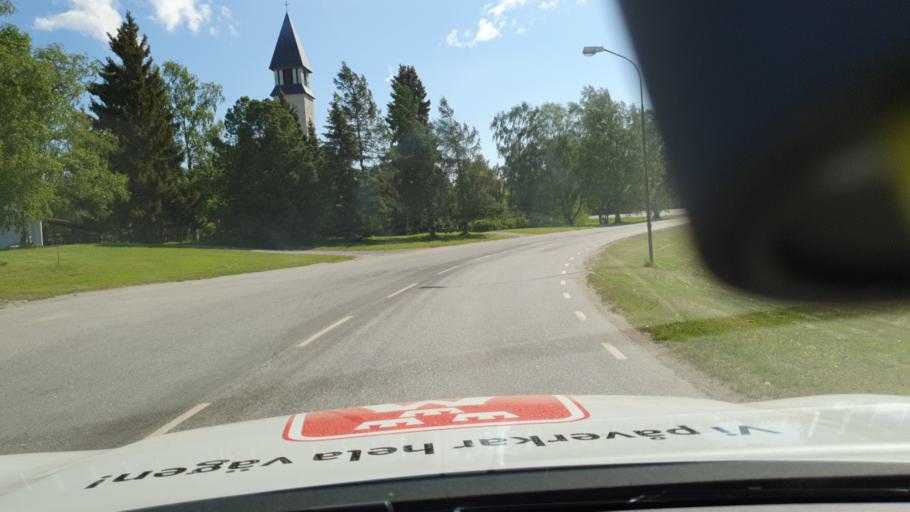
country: SE
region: Vaesterbotten
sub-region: Skelleftea Kommun
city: Burtraesk
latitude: 64.5176
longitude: 20.6612
